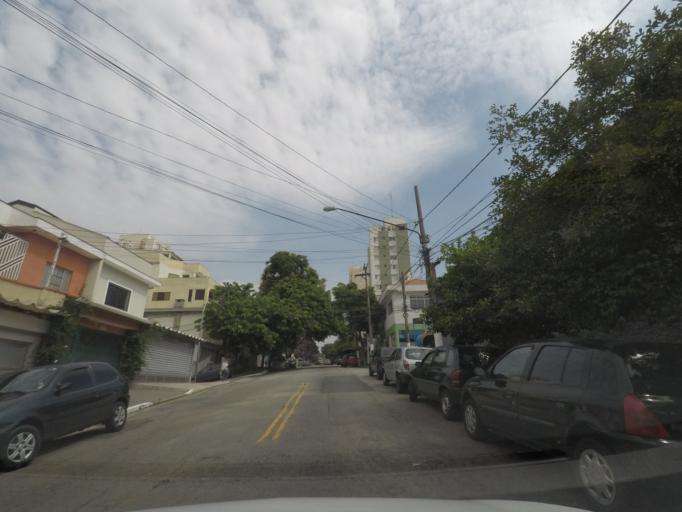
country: BR
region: Sao Paulo
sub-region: Diadema
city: Diadema
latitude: -23.6196
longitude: -46.6358
